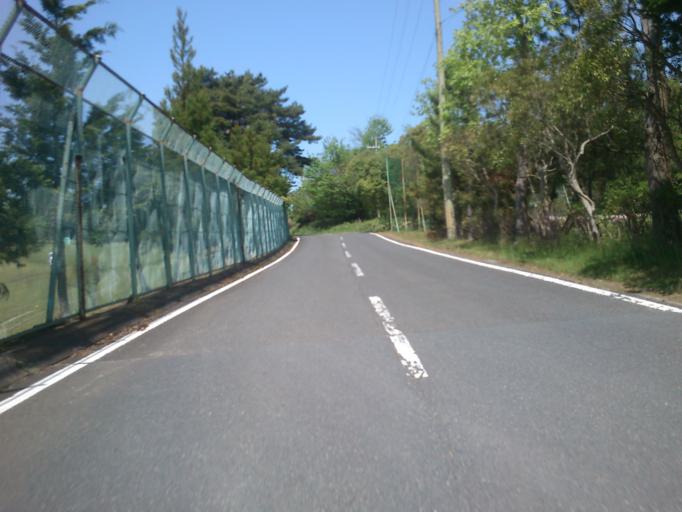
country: JP
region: Kyoto
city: Miyazu
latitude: 35.6269
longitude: 135.2235
